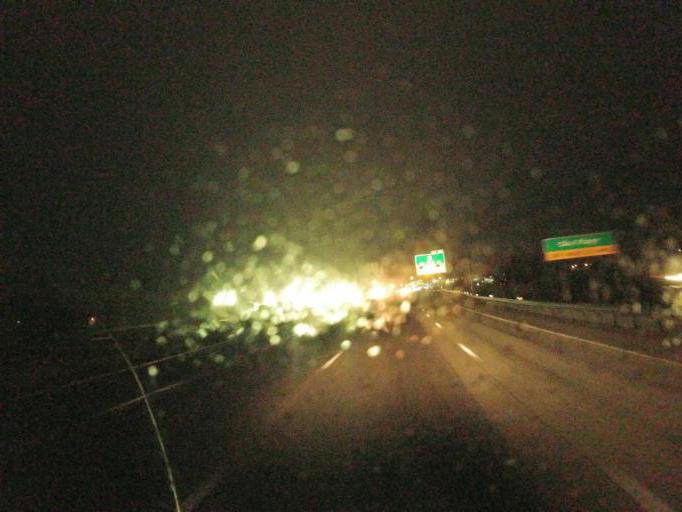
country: US
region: Missouri
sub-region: Saint Louis County
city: Eureka
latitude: 38.5047
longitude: -90.6689
